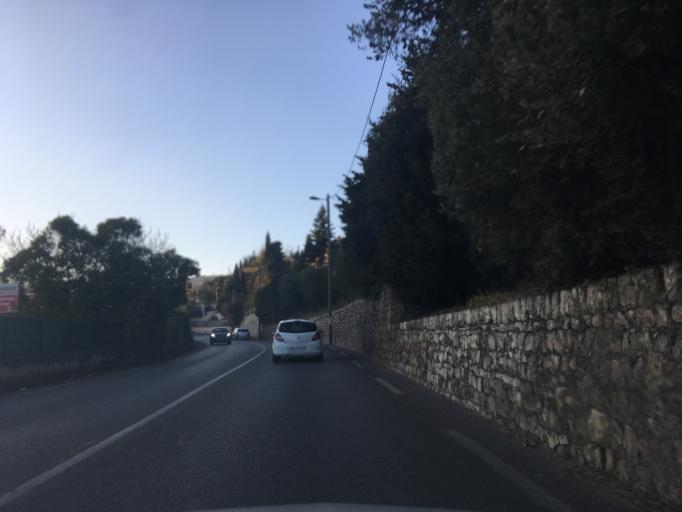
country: FR
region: Provence-Alpes-Cote d'Azur
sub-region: Departement des Alpes-Maritimes
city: Peymeinade
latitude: 43.6447
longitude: 6.8968
